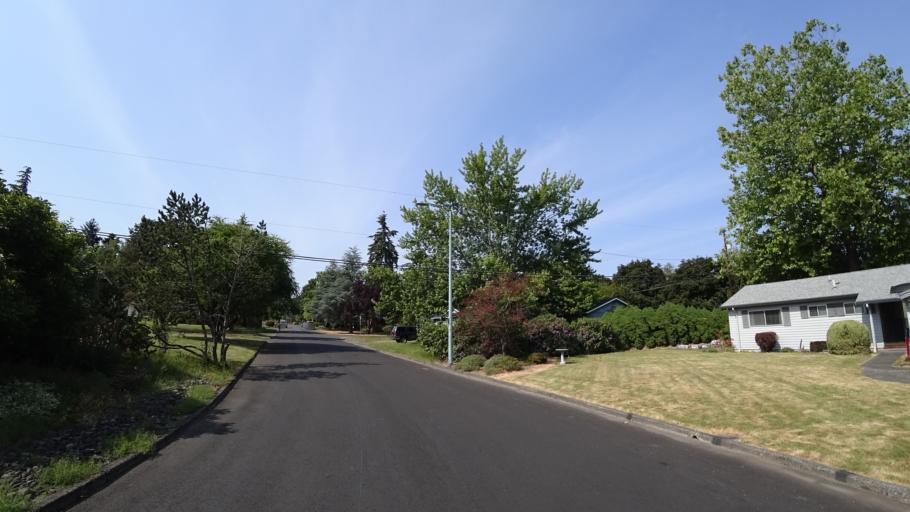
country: US
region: Oregon
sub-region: Washington County
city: Cedar Mill
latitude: 45.5082
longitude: -122.8232
